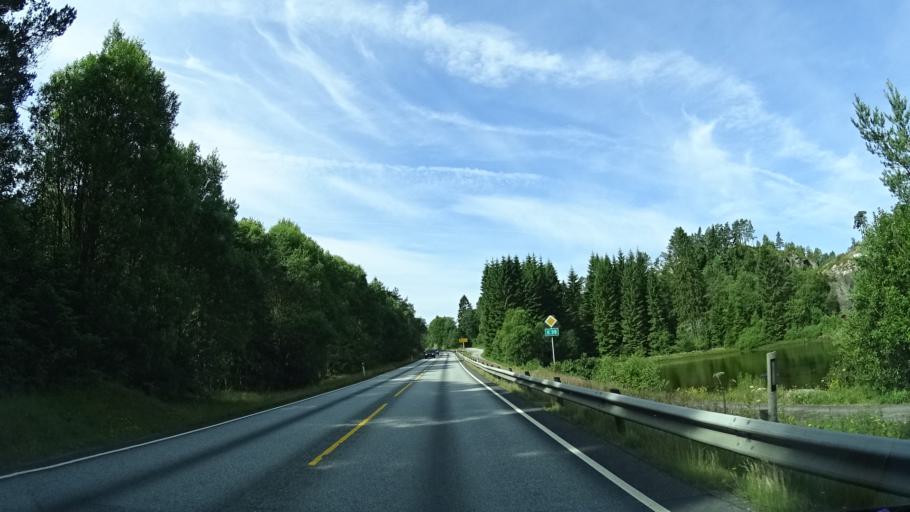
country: NO
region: Hordaland
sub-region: Sveio
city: Sveio
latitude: 59.5836
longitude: 5.4409
